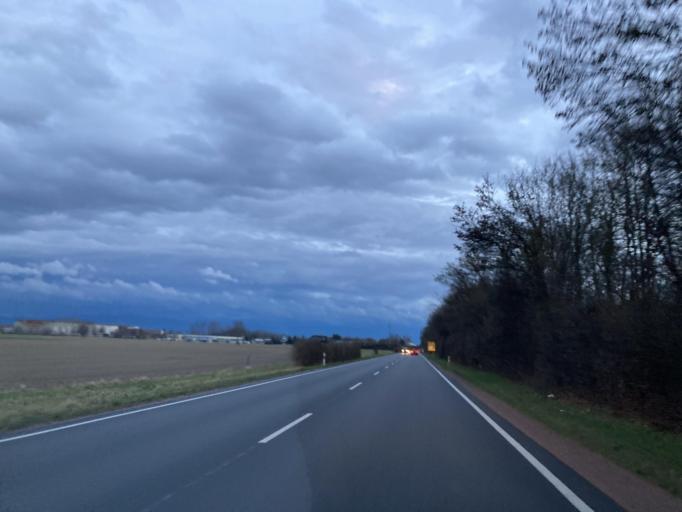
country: DE
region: Baden-Wuerttemberg
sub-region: Freiburg Region
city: Breisach am Rhein
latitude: 48.0386
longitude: 7.5897
